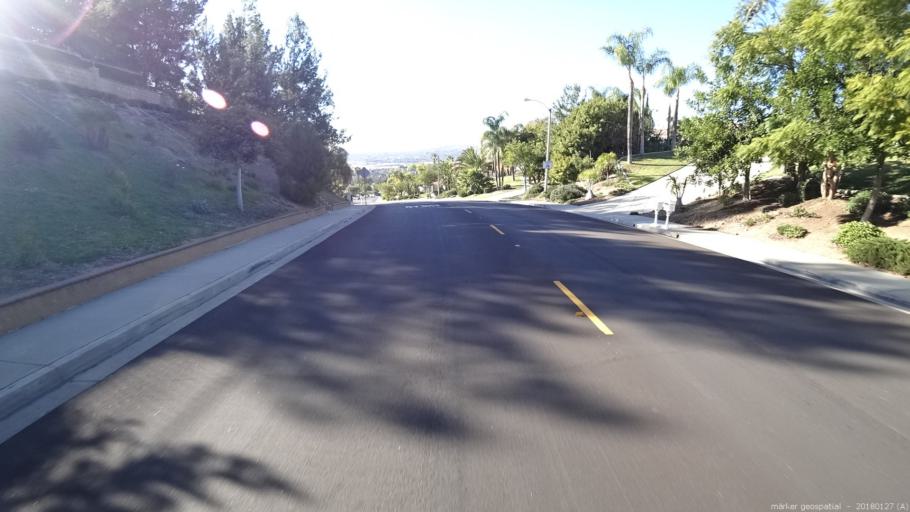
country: US
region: California
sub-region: Los Angeles County
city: Diamond Bar
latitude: 34.0155
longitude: -117.7992
